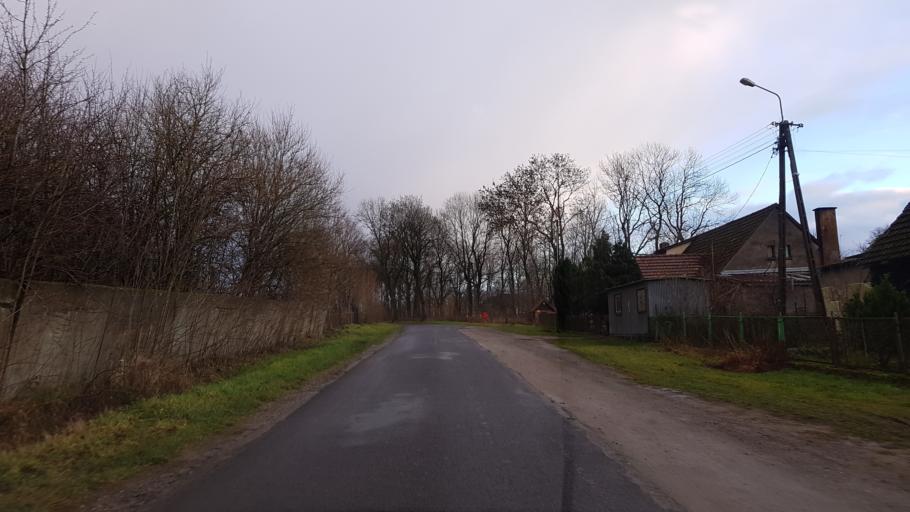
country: PL
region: West Pomeranian Voivodeship
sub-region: Powiat swidwinski
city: Rabino
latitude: 53.9467
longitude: 15.9176
